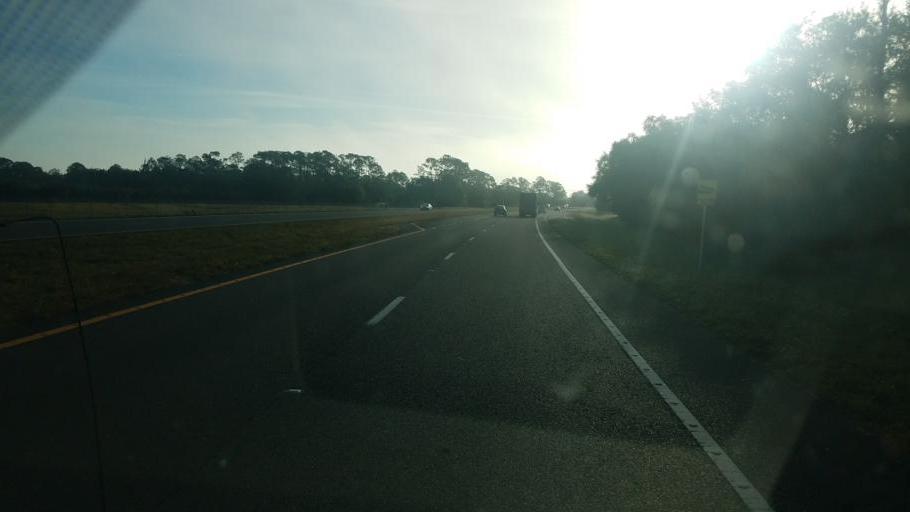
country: US
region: Florida
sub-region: Osceola County
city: Saint Cloud
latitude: 28.2417
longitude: -81.2048
